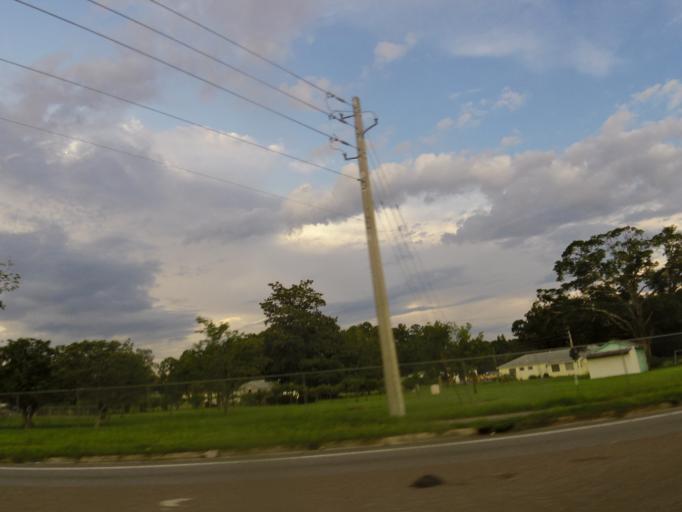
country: US
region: Florida
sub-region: Clay County
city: Bellair-Meadowbrook Terrace
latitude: 30.2686
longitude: -81.7734
